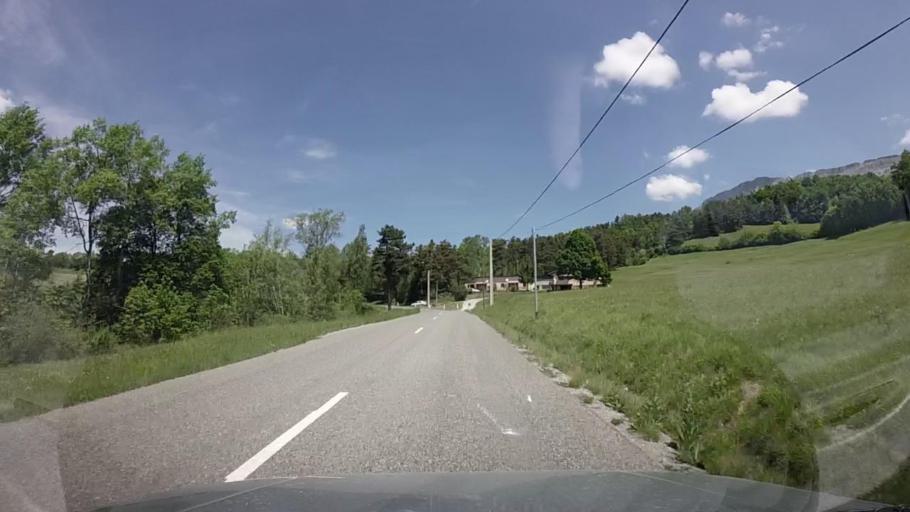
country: FR
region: Provence-Alpes-Cote d'Azur
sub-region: Departement des Alpes-de-Haute-Provence
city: Seyne-les-Alpes
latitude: 44.3793
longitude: 6.3519
